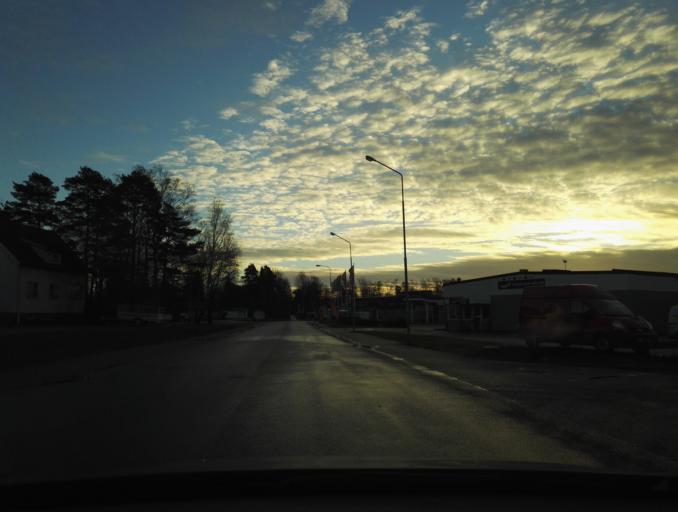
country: SE
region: Kronoberg
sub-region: Vaxjo Kommun
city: Vaexjoe
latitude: 56.8910
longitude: 14.7802
